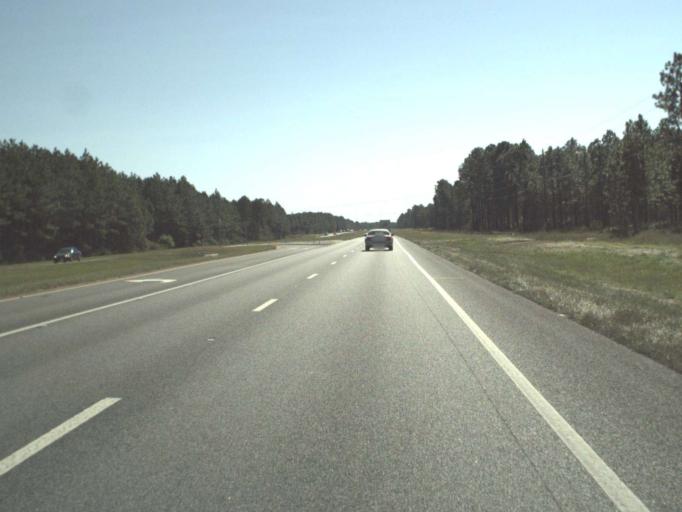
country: US
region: Florida
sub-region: Walton County
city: Seaside
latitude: 30.3435
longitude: -86.0730
